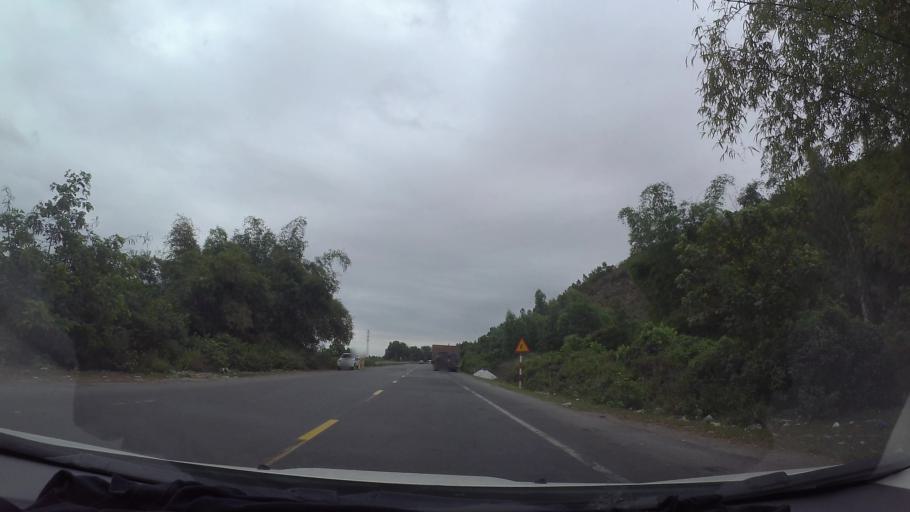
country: VN
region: Da Nang
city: Lien Chieu
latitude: 16.1211
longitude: 108.1015
